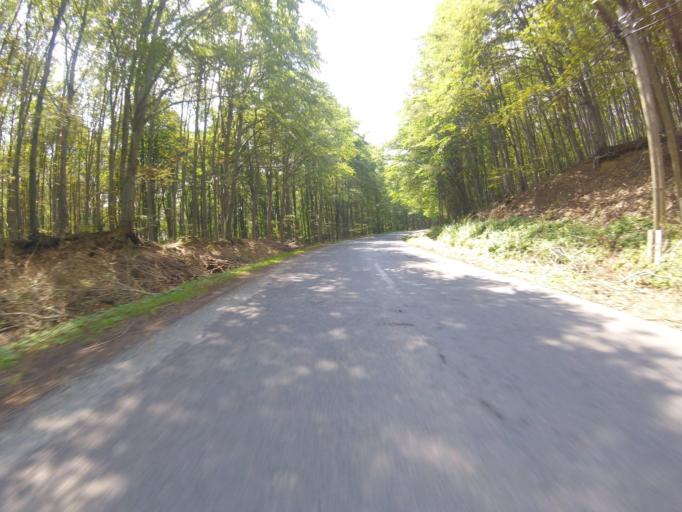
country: HU
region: Nograd
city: Batonyterenye
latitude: 47.8983
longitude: 19.8824
